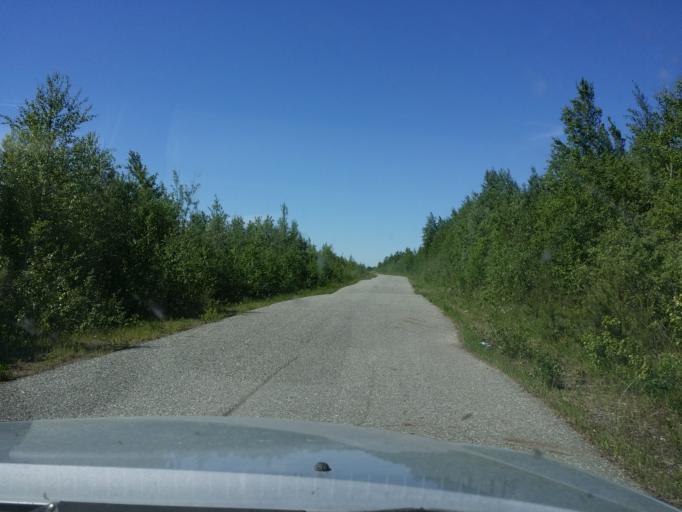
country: RU
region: Khanty-Mansiyskiy Avtonomnyy Okrug
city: Surgut
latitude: 61.4162
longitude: 73.8305
